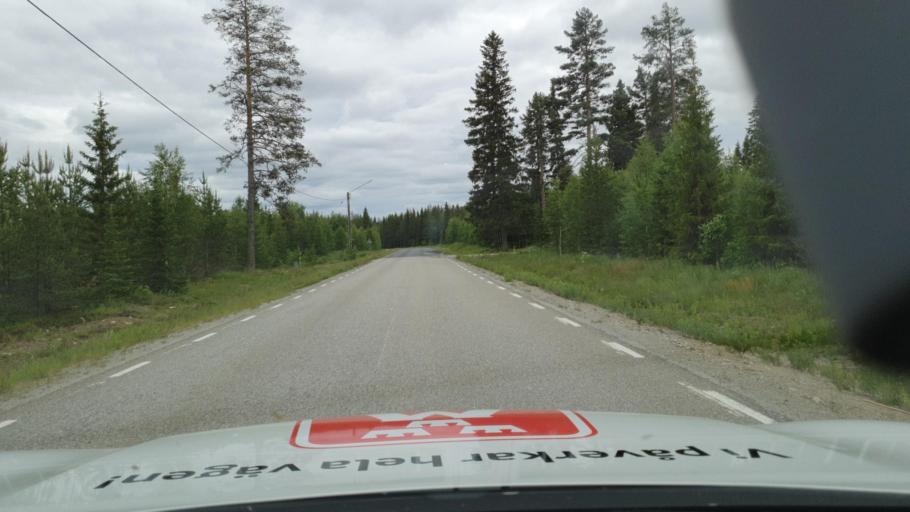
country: SE
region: Vaesterbotten
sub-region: Lycksele Kommun
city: Soderfors
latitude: 64.2909
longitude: 18.1826
